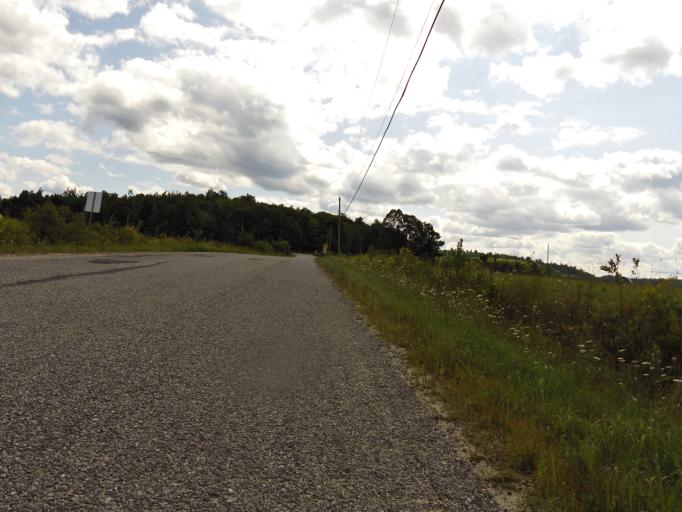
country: CA
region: Quebec
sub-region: Outaouais
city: Wakefield
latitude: 45.8053
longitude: -75.9832
